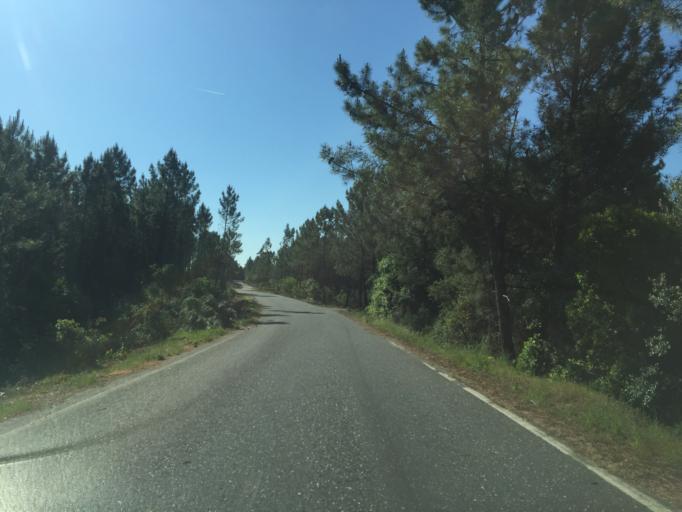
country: PT
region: Coimbra
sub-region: Pampilhosa da Serra
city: Pampilhosa da Serra
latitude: 40.0551
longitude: -7.8499
